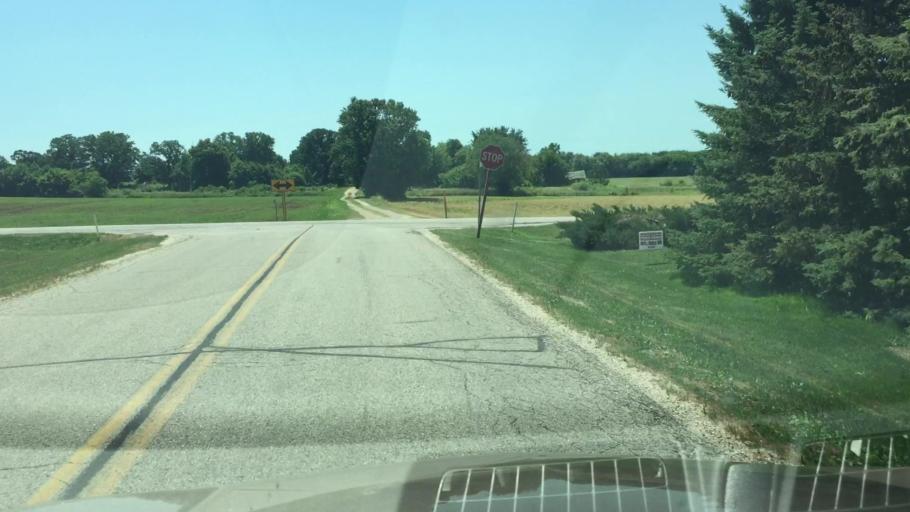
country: US
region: Wisconsin
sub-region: Fond du Lac County
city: Saint Peter
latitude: 43.9369
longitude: -88.3113
